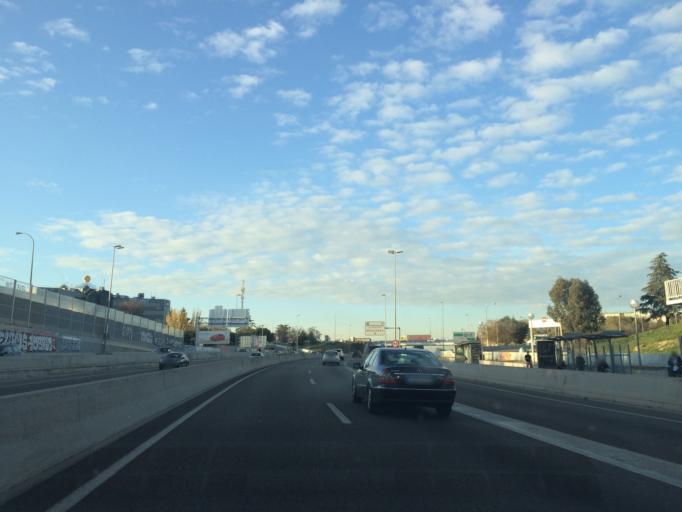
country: ES
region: Madrid
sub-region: Provincia de Madrid
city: Tetuan de las Victorias
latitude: 40.4874
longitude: -3.6968
